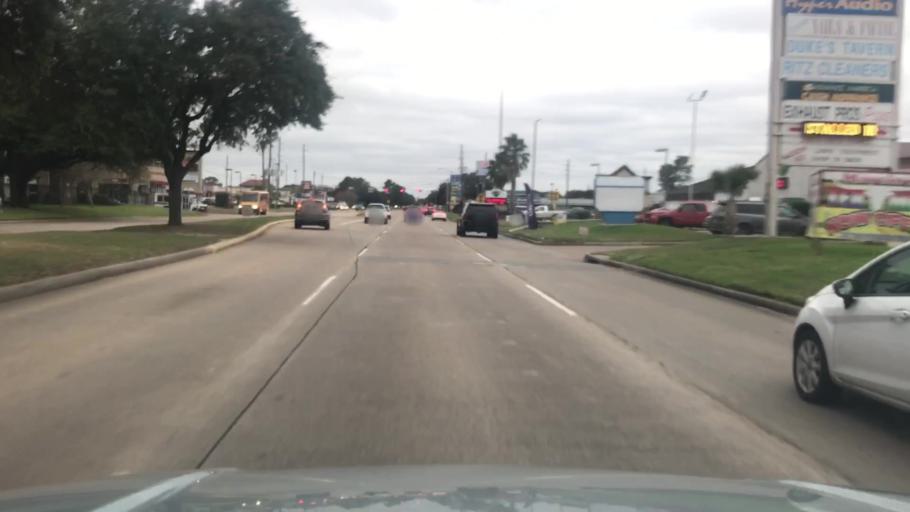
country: US
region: Texas
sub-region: Fort Bend County
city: Cinco Ranch
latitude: 29.7665
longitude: -95.7517
